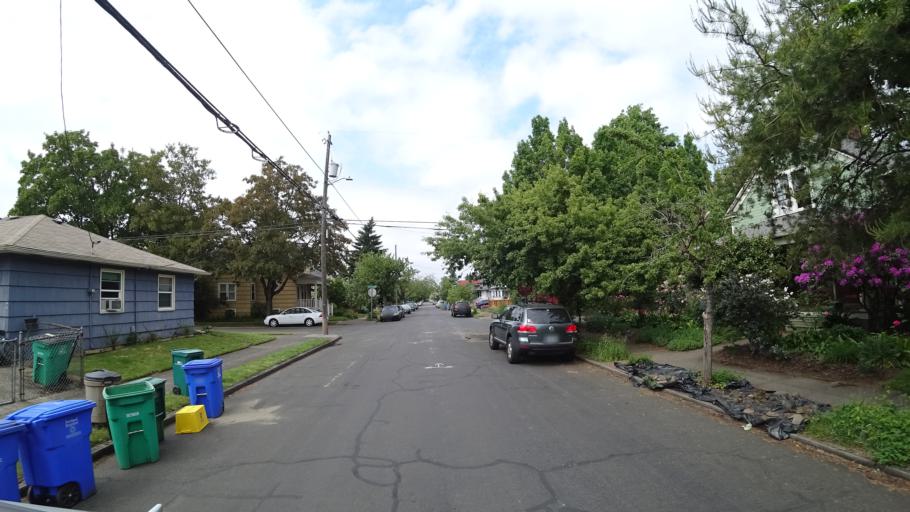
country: US
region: Oregon
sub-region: Multnomah County
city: Portland
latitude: 45.5571
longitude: -122.6537
